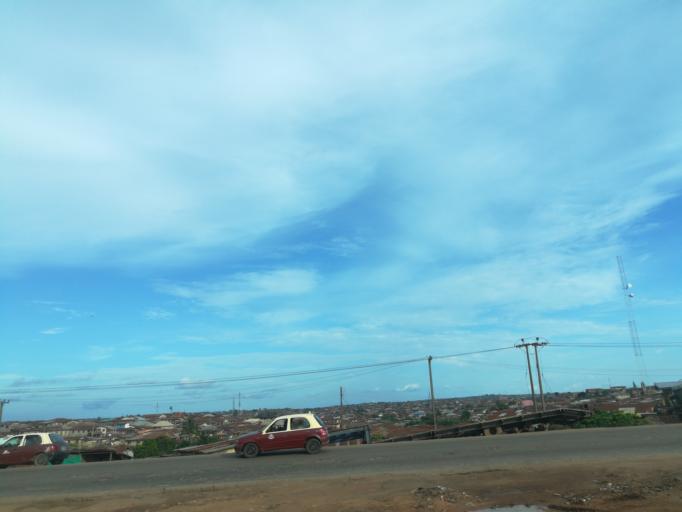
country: NG
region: Oyo
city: Ibadan
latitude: 7.3698
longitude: 3.9286
